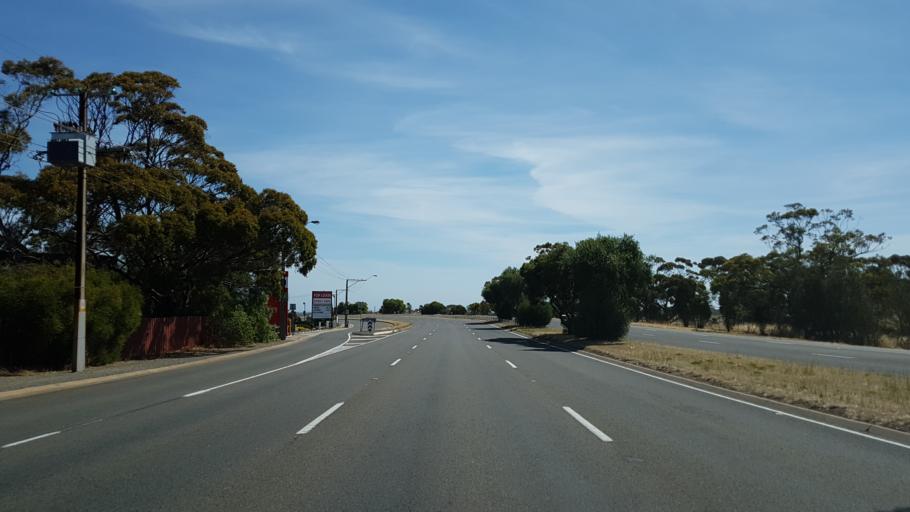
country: AU
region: South Australia
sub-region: Marion
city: Trott Park
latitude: -35.0627
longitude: 138.5570
